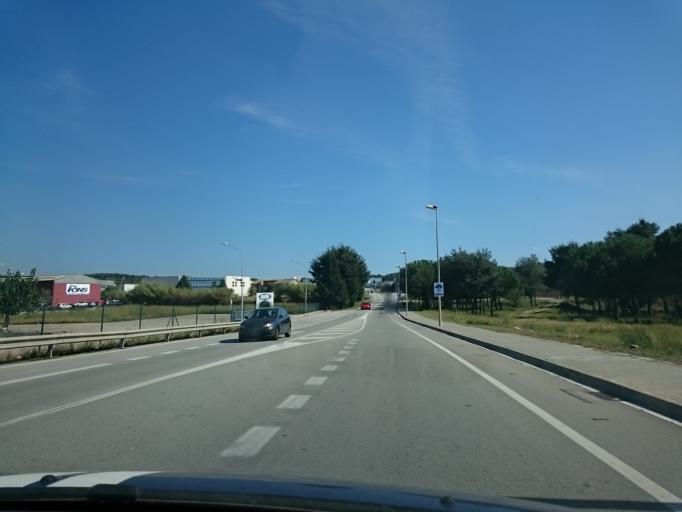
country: ES
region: Catalonia
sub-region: Provincia de Barcelona
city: Llica de Vall
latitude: 41.5865
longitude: 2.2464
